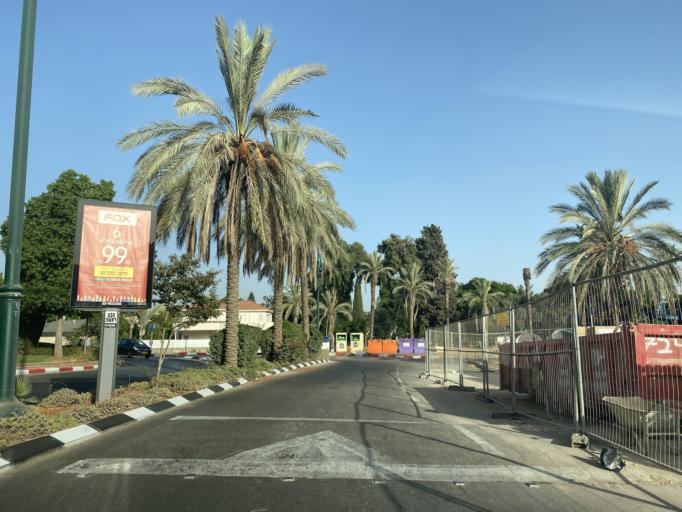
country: IL
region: Central District
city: Kfar Saba
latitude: 32.1632
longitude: 34.9096
